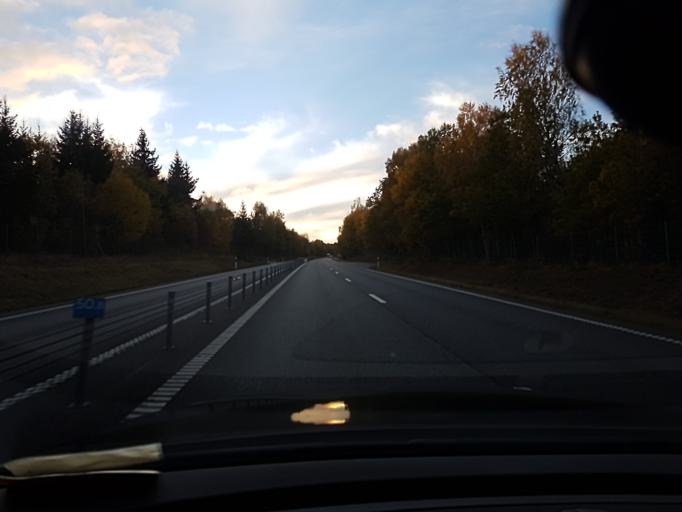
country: SE
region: Kronoberg
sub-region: Ljungby Kommun
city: Lagan
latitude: 56.8513
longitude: 14.0311
